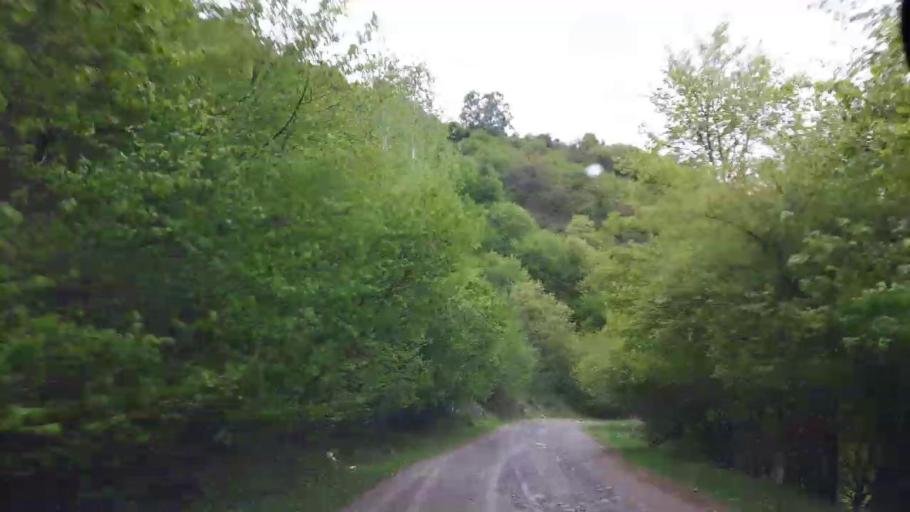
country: GE
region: Shida Kartli
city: Gori
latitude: 41.8610
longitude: 43.9515
